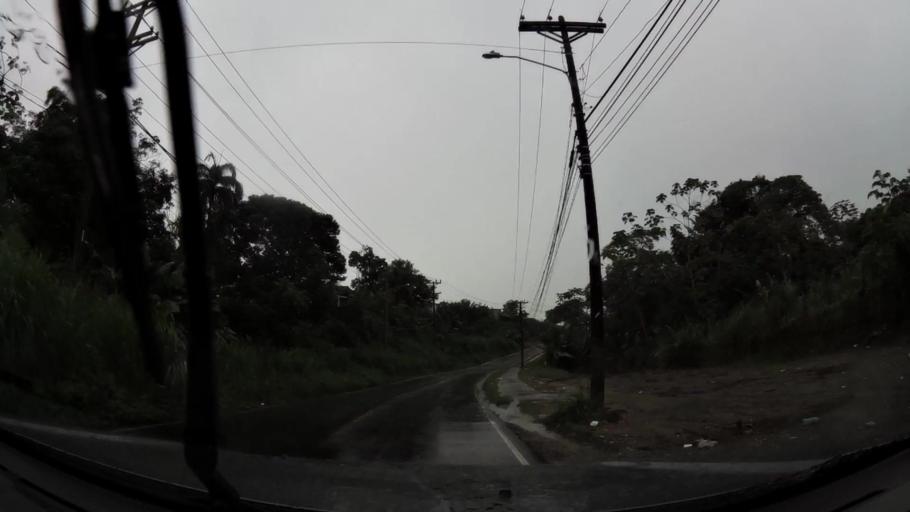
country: PA
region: Colon
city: Puerto Pilon
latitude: 9.3565
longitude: -79.8017
